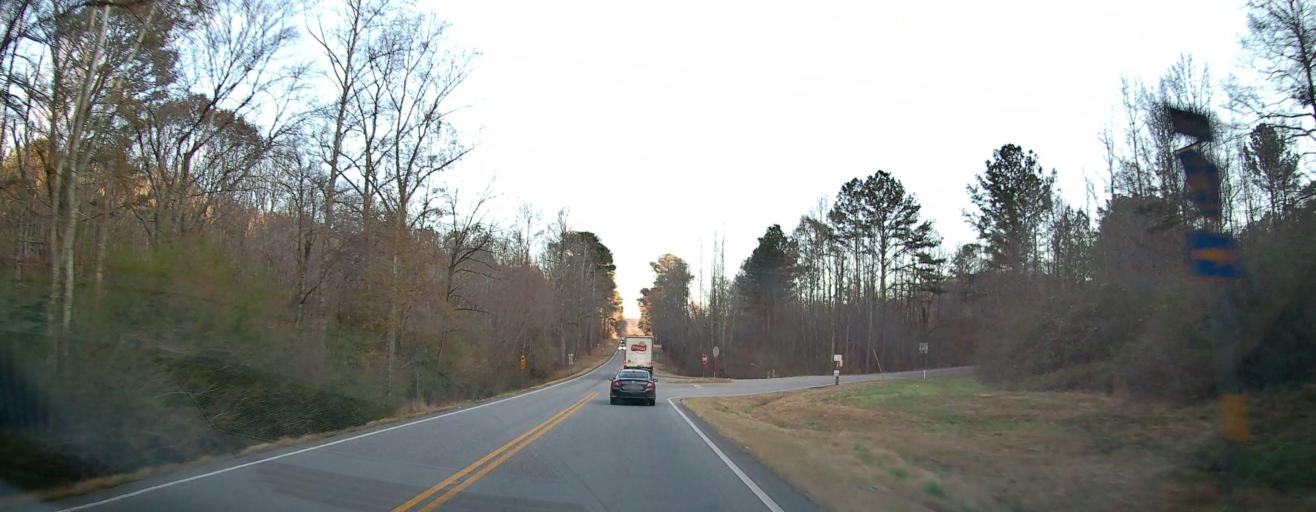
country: US
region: Alabama
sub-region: Blount County
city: Oneonta
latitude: 34.0784
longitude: -86.3373
